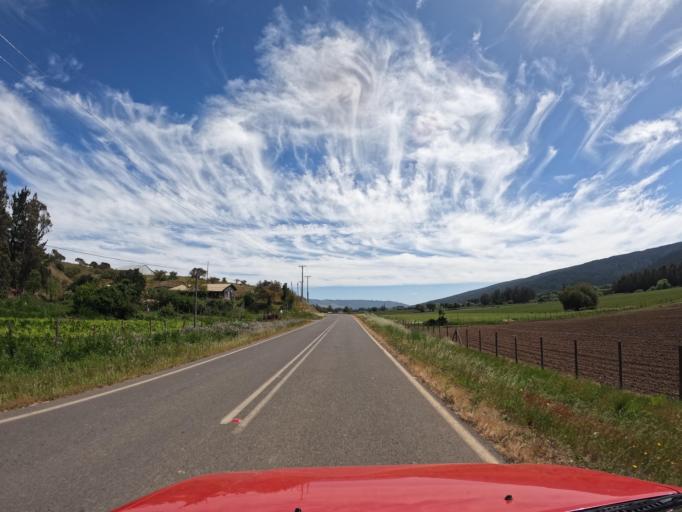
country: CL
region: Maule
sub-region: Provincia de Talca
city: Constitucion
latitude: -34.9989
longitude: -72.0240
